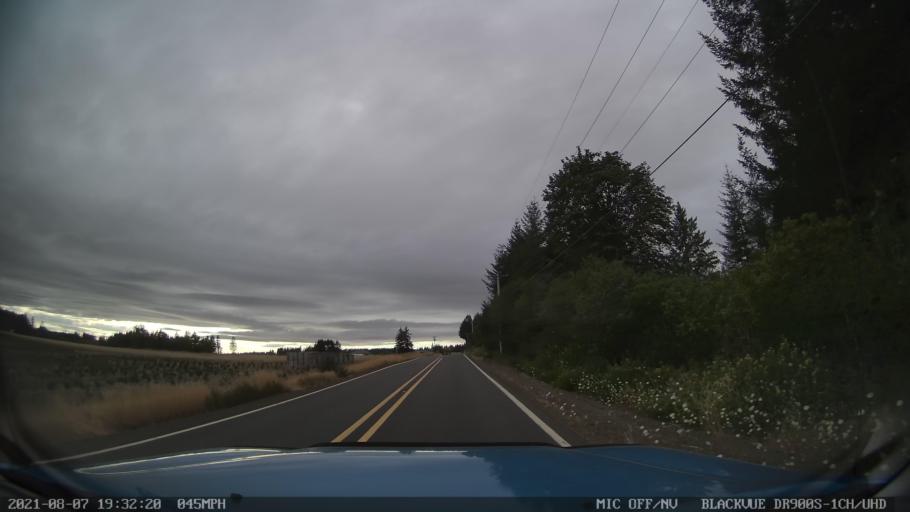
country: US
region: Oregon
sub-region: Linn County
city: Lyons
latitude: 44.8991
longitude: -122.6424
